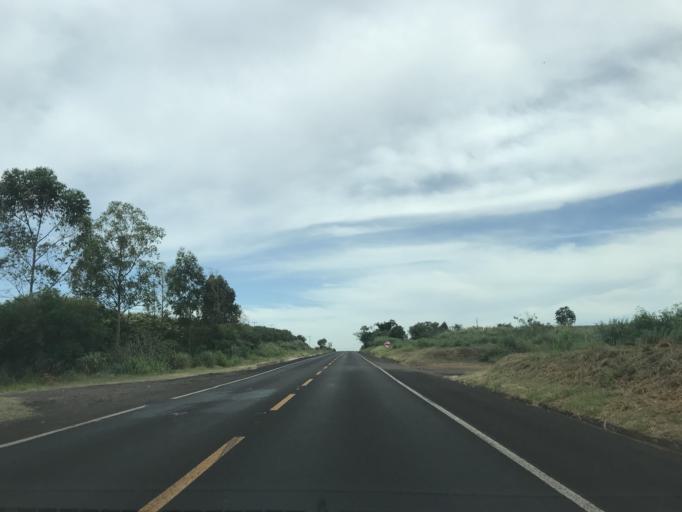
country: BR
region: Parana
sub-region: Paranavai
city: Paranavai
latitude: -23.0171
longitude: -52.5069
